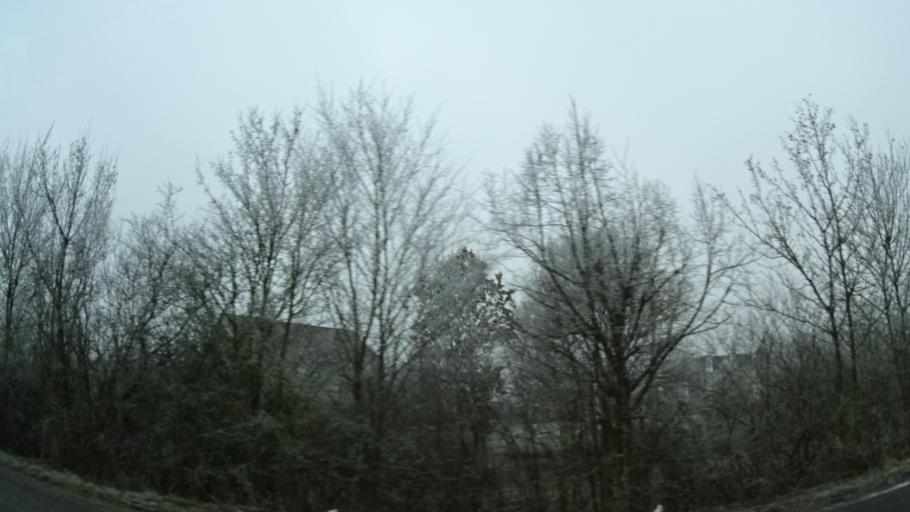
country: DE
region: Bavaria
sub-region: Regierungsbezirk Unterfranken
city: Albertshofen
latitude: 49.7486
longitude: 10.1782
